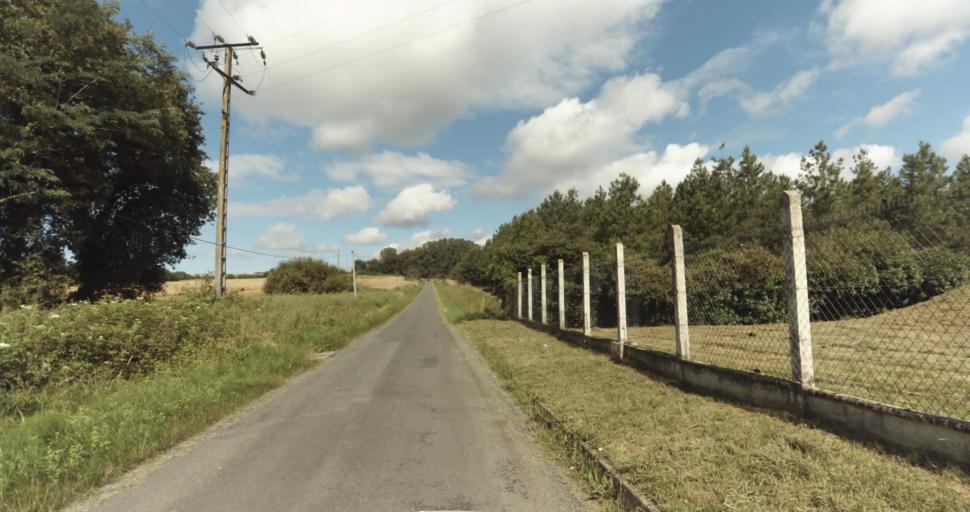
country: FR
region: Aquitaine
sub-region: Departement de la Gironde
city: Bazas
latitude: 44.4481
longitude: -0.1678
